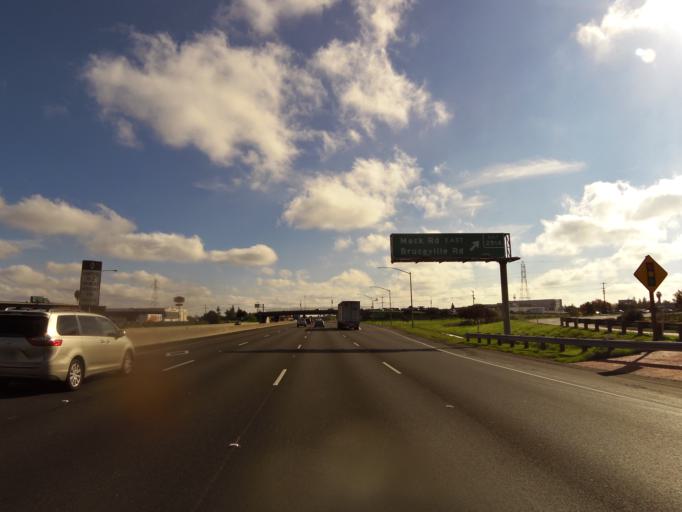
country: US
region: California
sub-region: Sacramento County
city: Florin
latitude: 38.4765
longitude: -121.4254
